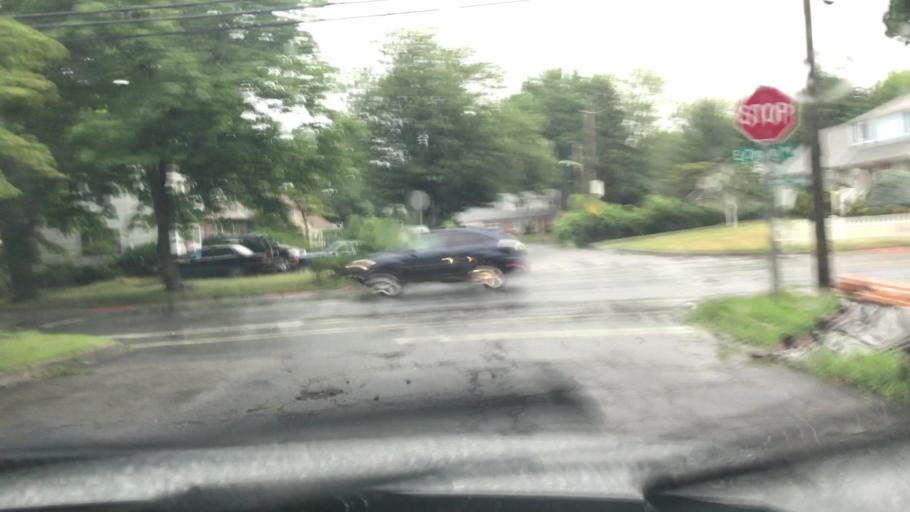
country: US
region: New Jersey
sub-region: Bergen County
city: Bergenfield
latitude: 40.9237
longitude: -73.9871
